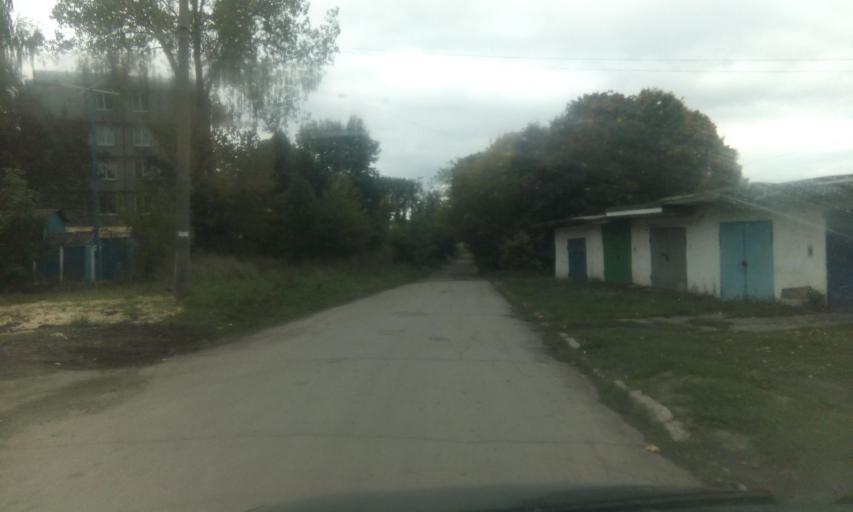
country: RU
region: Tula
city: Gritsovskiy
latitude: 54.1356
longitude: 38.1565
